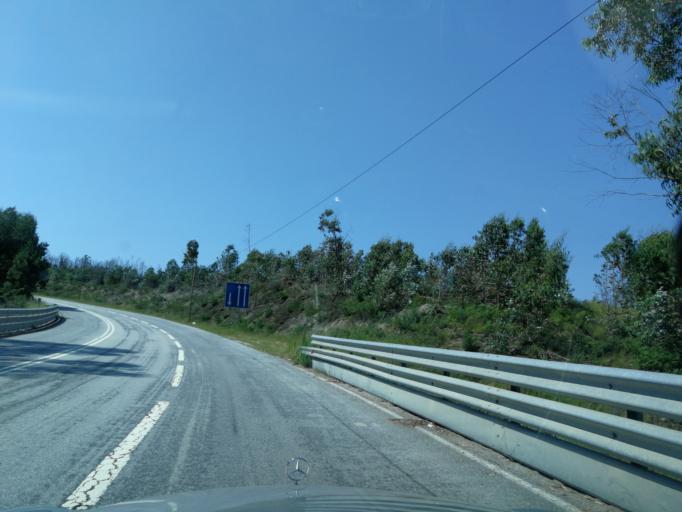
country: PT
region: Braga
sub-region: Braga
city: Adaufe
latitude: 41.5626
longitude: -8.3578
